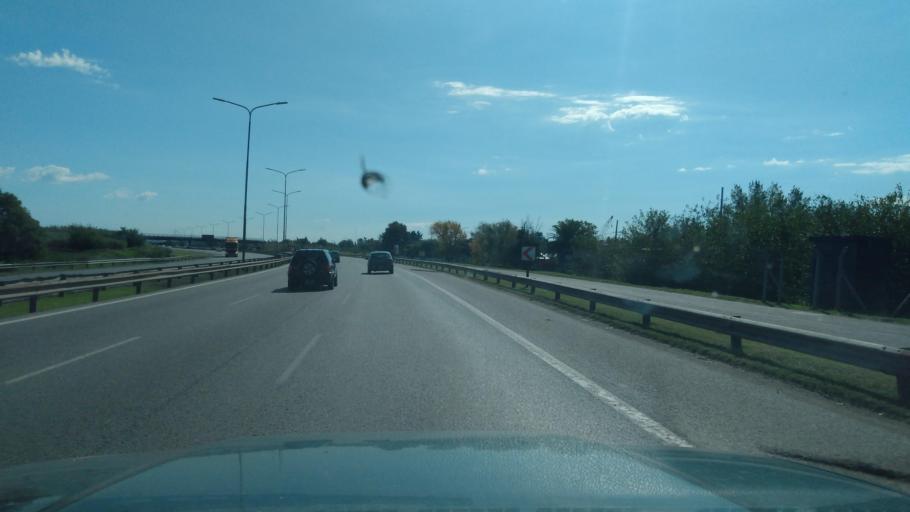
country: AR
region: Buenos Aires
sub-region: Partido de Tigre
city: Tigre
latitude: -34.4999
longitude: -58.5900
